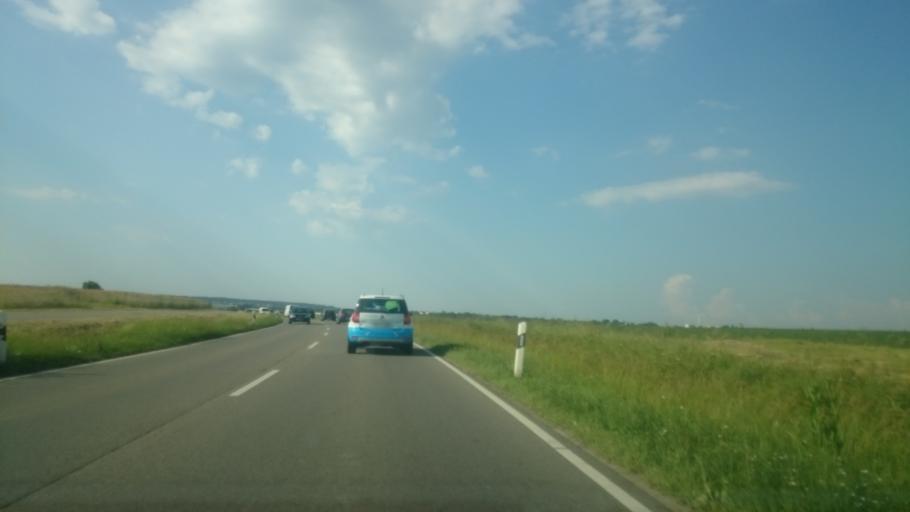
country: DE
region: Baden-Wuerttemberg
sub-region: Tuebingen Region
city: Nehren
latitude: 48.4409
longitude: 9.0805
